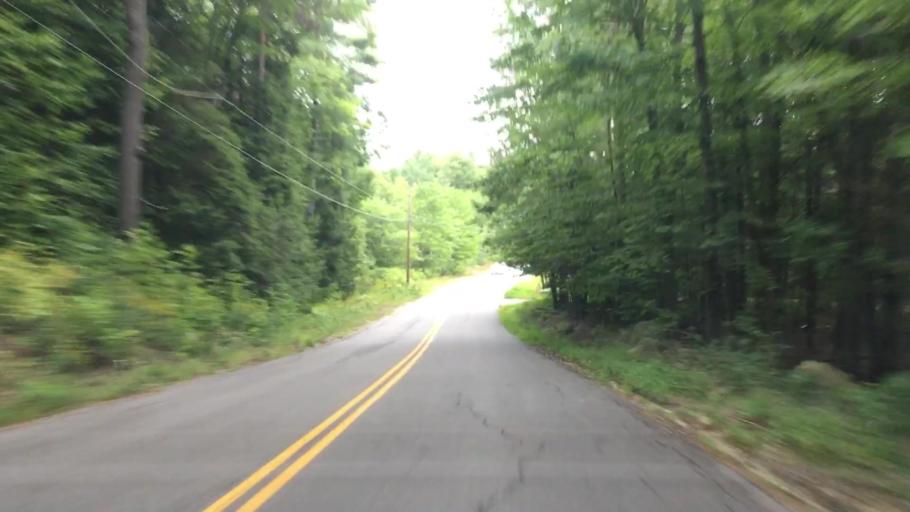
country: US
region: Maine
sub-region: Cumberland County
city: New Gloucester
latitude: 43.9038
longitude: -70.2109
